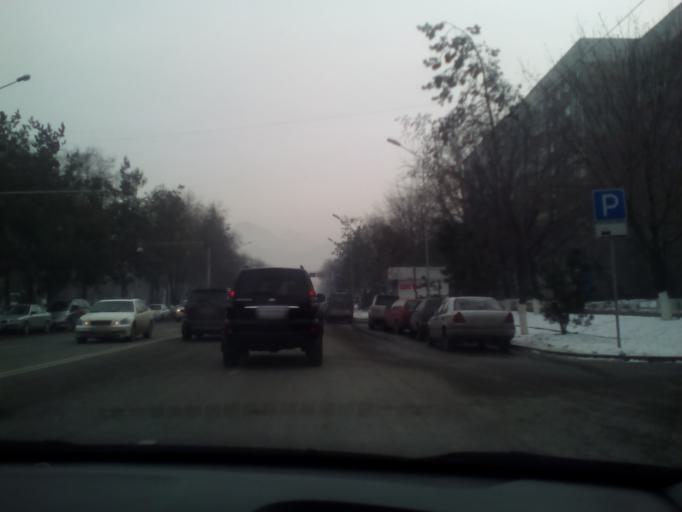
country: KZ
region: Almaty Qalasy
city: Almaty
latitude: 43.2346
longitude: 76.8314
